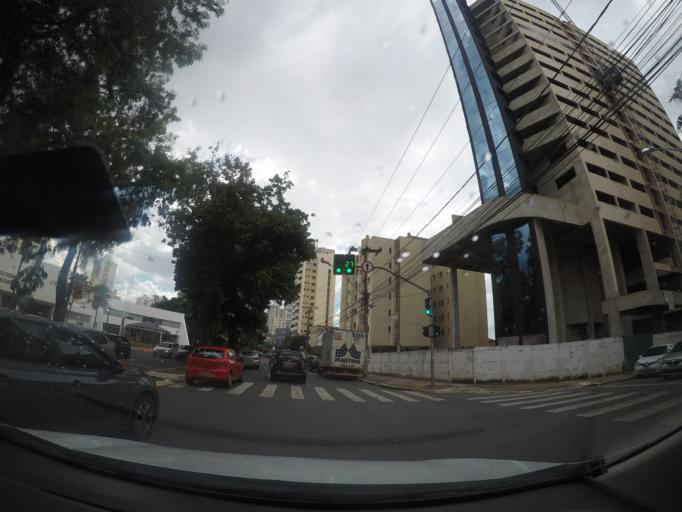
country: BR
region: Goias
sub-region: Goiania
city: Goiania
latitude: -16.6796
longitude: -49.2605
